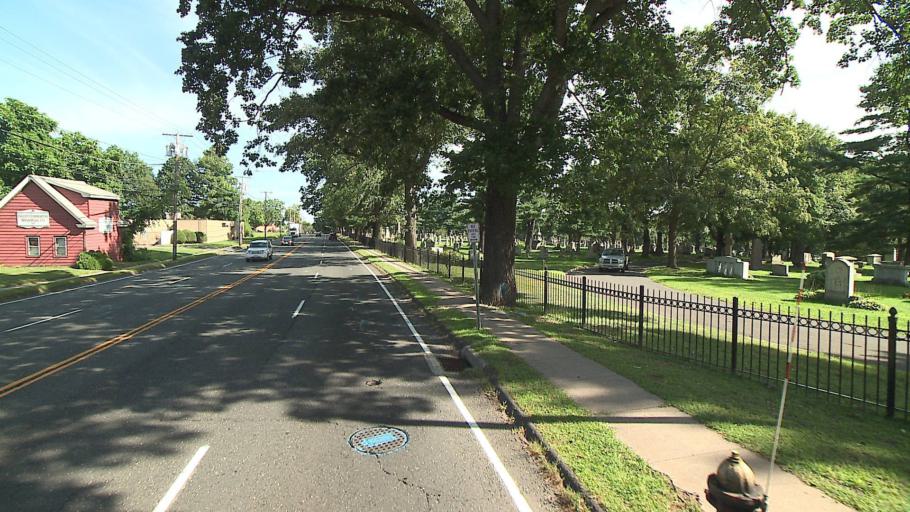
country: US
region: Connecticut
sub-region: Hartford County
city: Blue Hills
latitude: 41.8125
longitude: -72.6947
